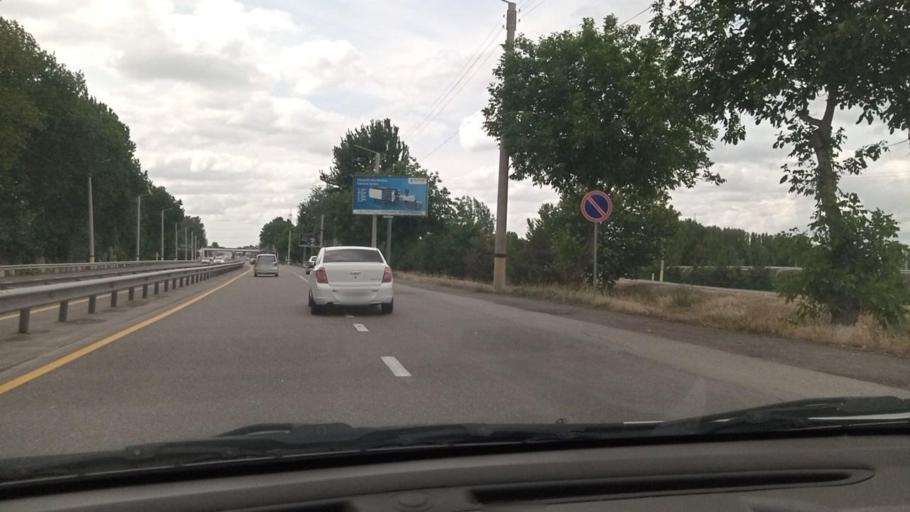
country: UZ
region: Toshkent Shahri
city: Bektemir
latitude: 41.2414
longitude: 69.4002
